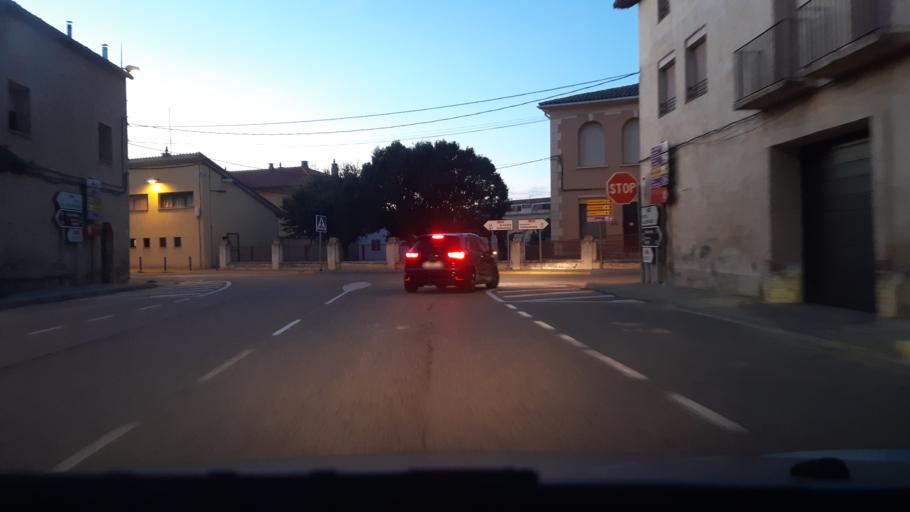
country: ES
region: Aragon
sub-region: Provincia de Teruel
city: Calaceite
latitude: 41.0138
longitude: 0.1869
